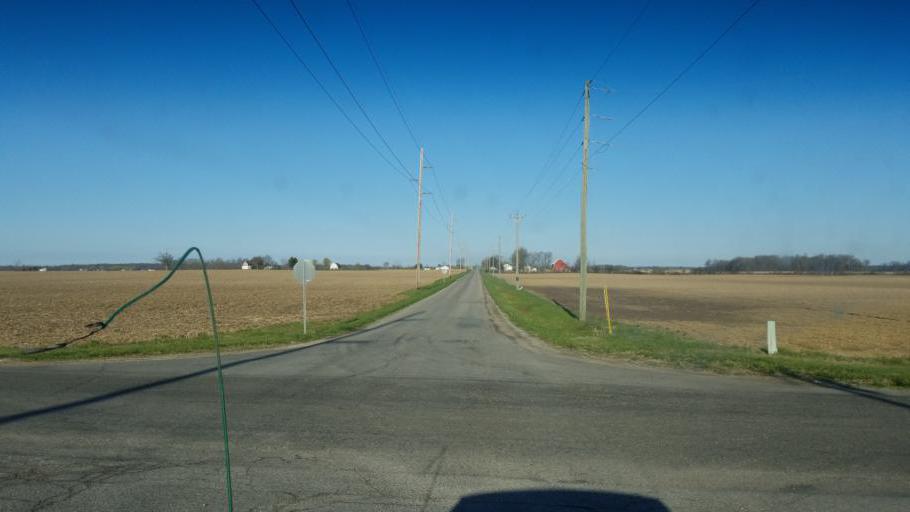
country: US
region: Ohio
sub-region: Union County
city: Richwood
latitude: 40.4488
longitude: -83.3931
